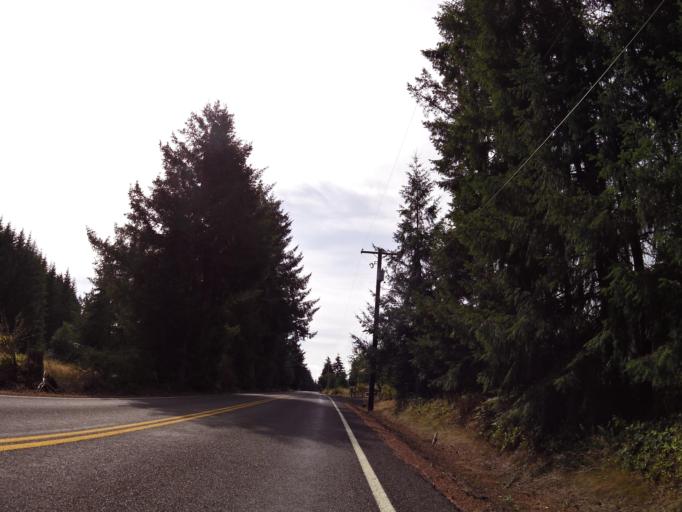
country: US
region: Washington
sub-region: Lewis County
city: Chehalis
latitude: 46.6022
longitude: -122.9712
